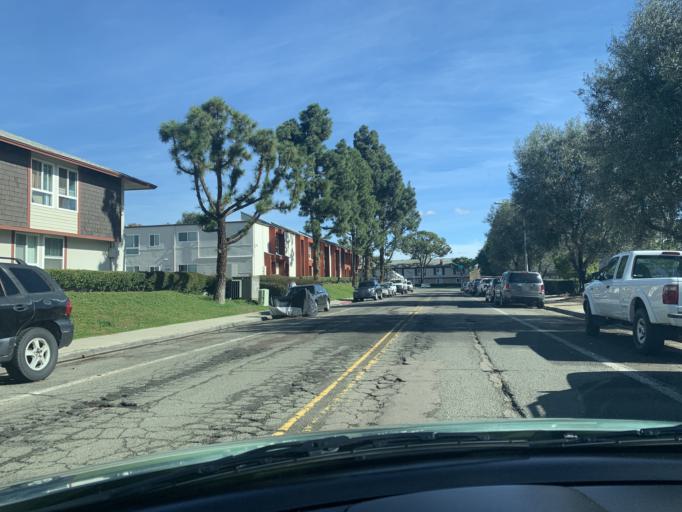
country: US
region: California
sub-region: San Diego County
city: San Diego
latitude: 32.8050
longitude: -117.1301
